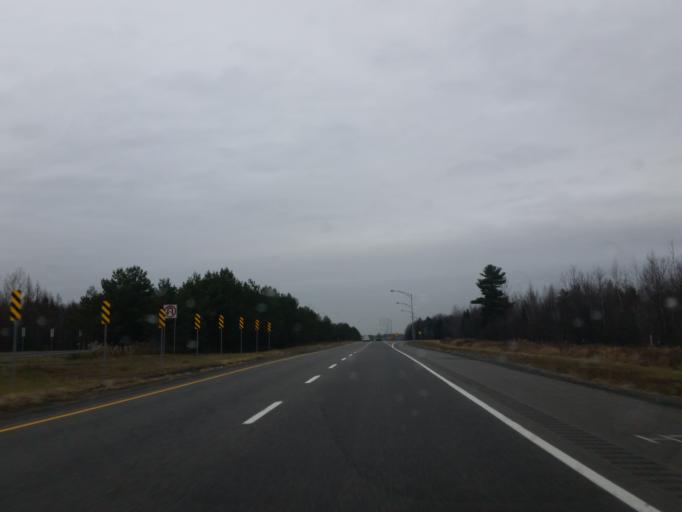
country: CA
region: Quebec
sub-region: Mauricie
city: Becancour
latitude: 46.5100
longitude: -72.2959
